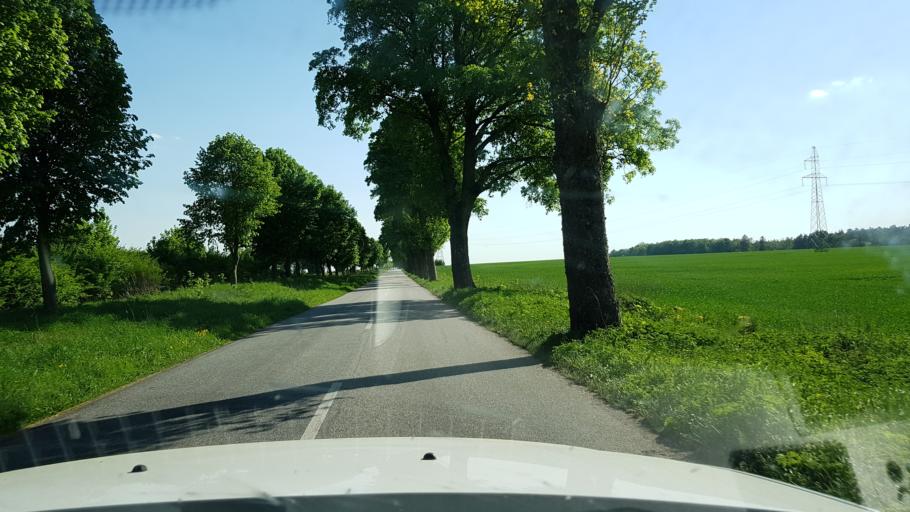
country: PL
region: West Pomeranian Voivodeship
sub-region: Powiat lobeski
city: Resko
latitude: 53.8022
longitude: 15.4171
